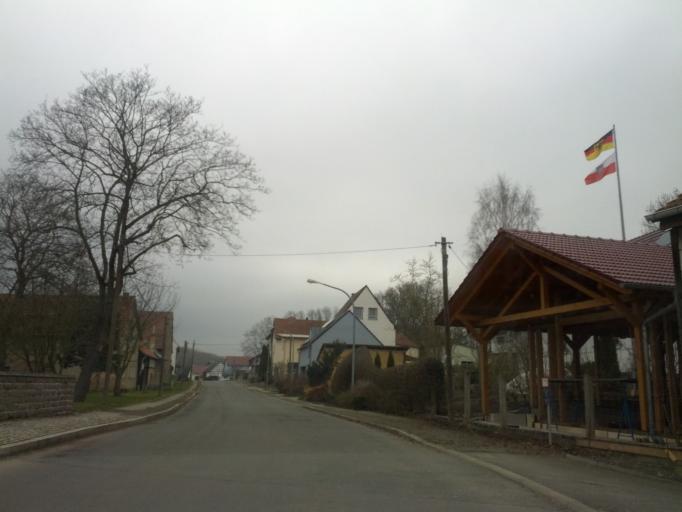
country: DE
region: Thuringia
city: Sonneborn
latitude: 51.0367
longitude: 10.5822
